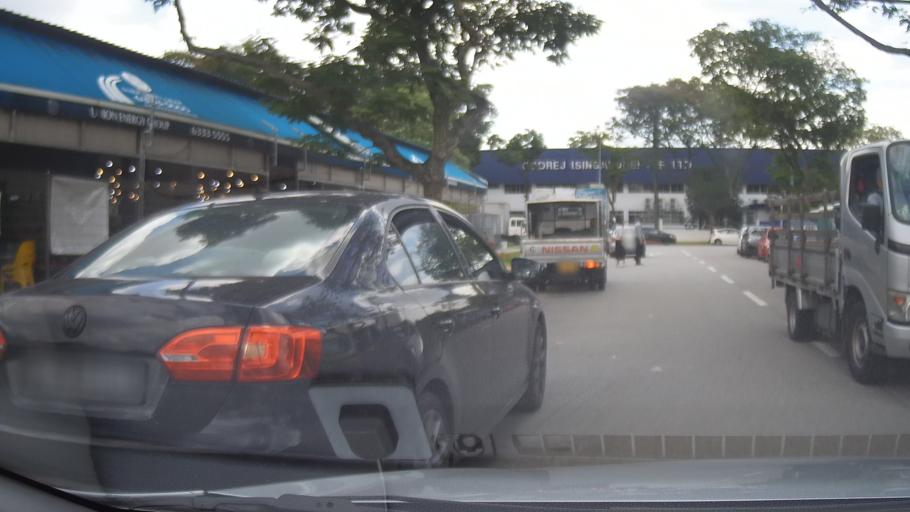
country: MY
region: Johor
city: Johor Bahru
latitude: 1.3252
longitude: 103.6899
